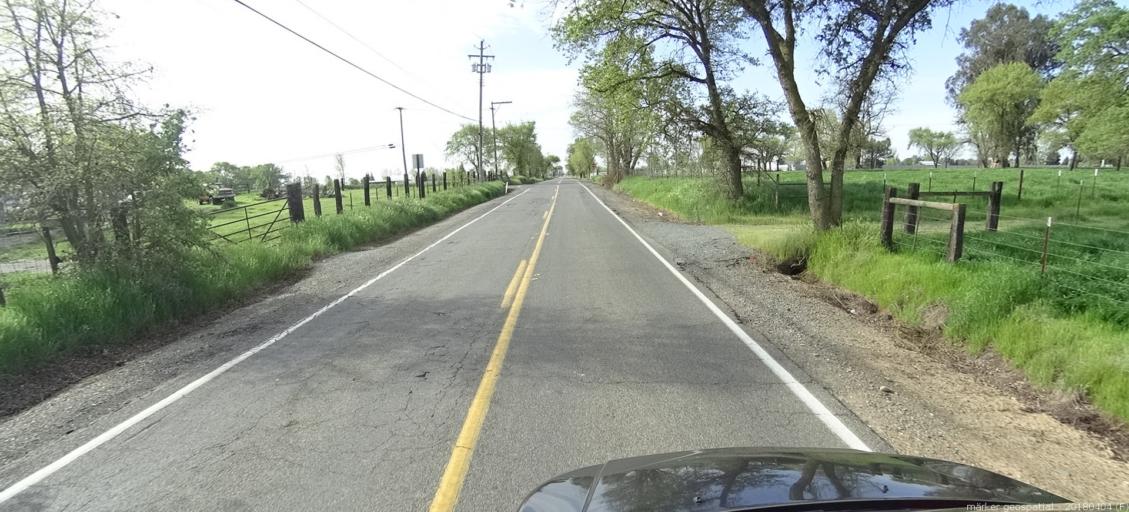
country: US
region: California
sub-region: Sacramento County
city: Herald
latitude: 38.2929
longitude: -121.2265
